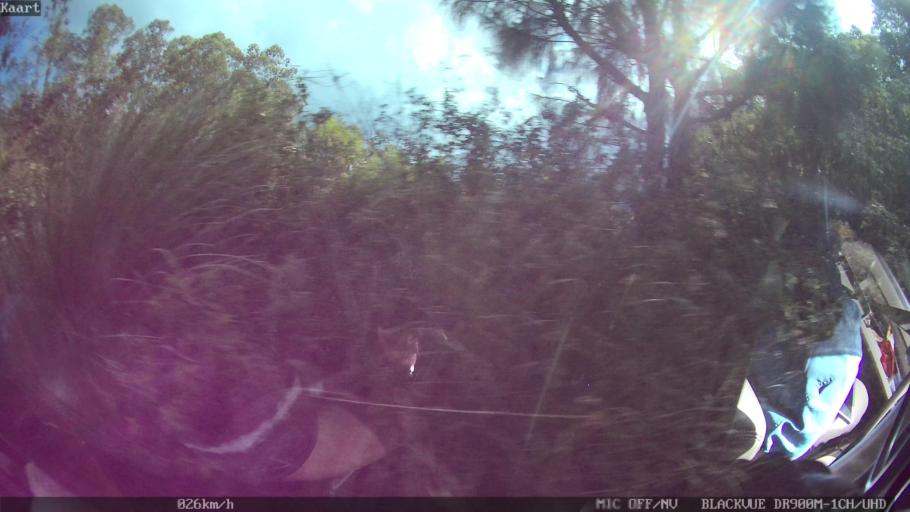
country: ID
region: Bali
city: Banjar Kedisan
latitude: -8.2172
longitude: 115.3670
